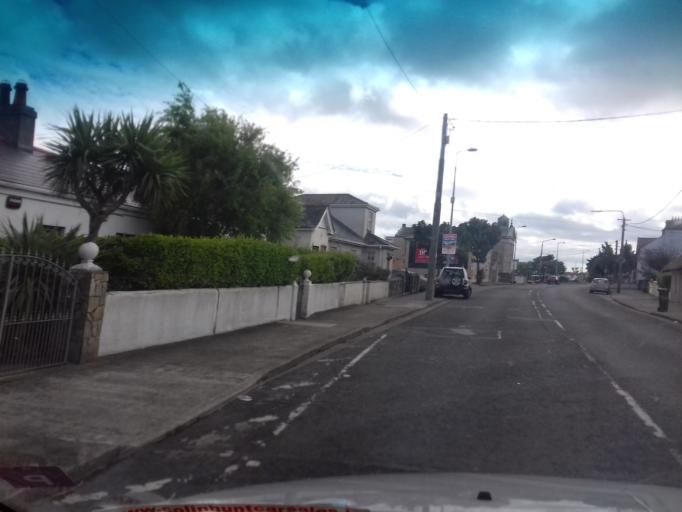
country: IE
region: Leinster
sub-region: Fingal County
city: Baldoyle
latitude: 53.4001
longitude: -6.1288
